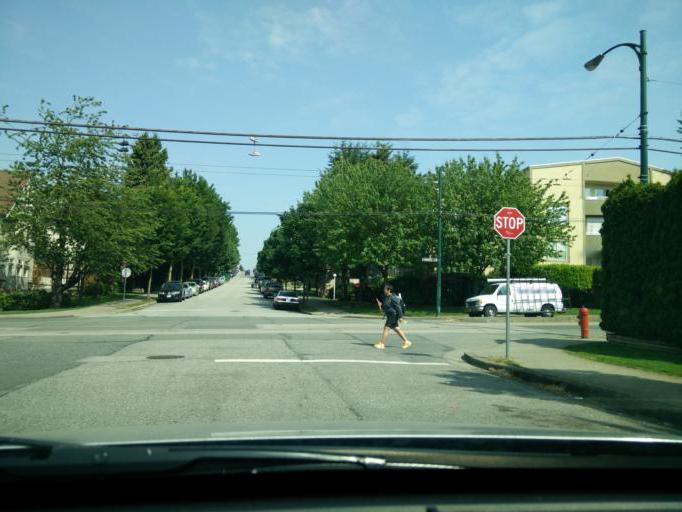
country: CA
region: British Columbia
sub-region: Fraser Valley Regional District
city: North Vancouver
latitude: 49.2803
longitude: -123.0708
